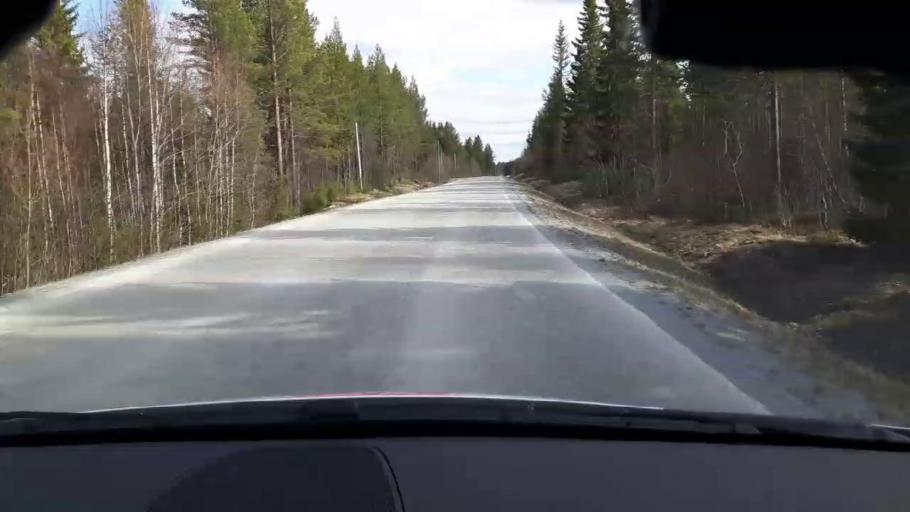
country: SE
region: Jaemtland
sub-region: Bergs Kommun
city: Hoverberg
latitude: 62.7497
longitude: 14.5753
